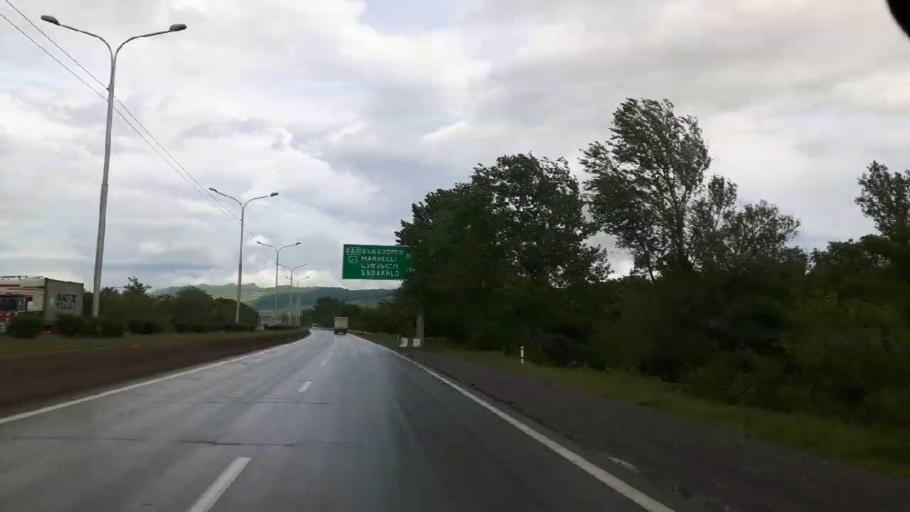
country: GE
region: Shida Kartli
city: Kaspi
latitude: 41.9117
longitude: 44.5646
